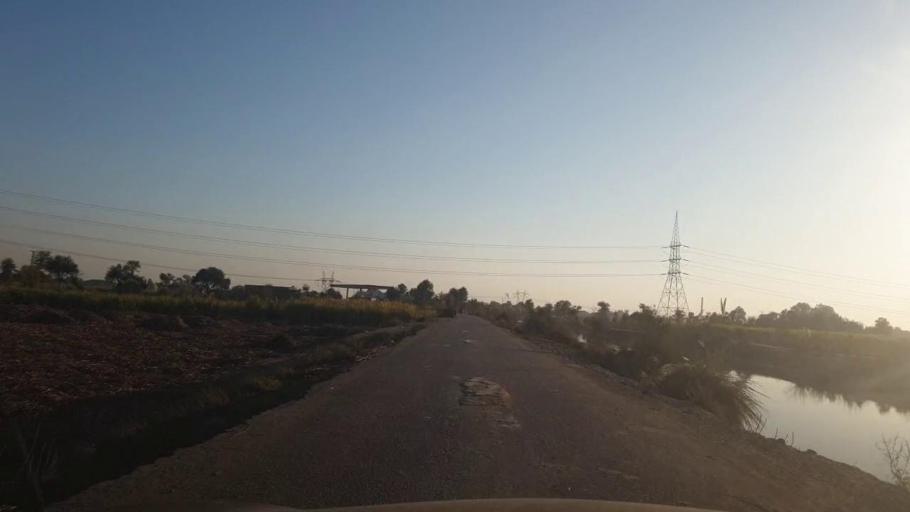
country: PK
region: Sindh
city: Mirpur Mathelo
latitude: 27.9909
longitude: 69.4652
